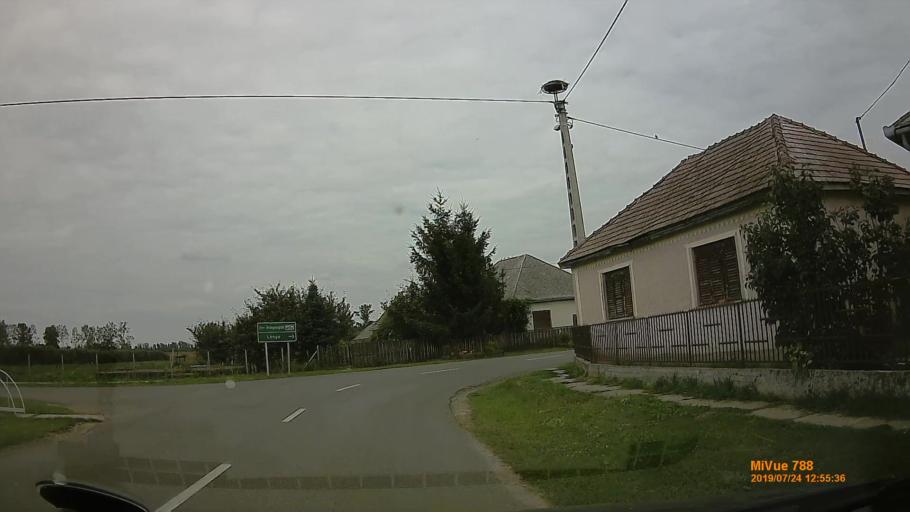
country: HU
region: Szabolcs-Szatmar-Bereg
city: Aranyosapati
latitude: 48.2251
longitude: 22.2908
